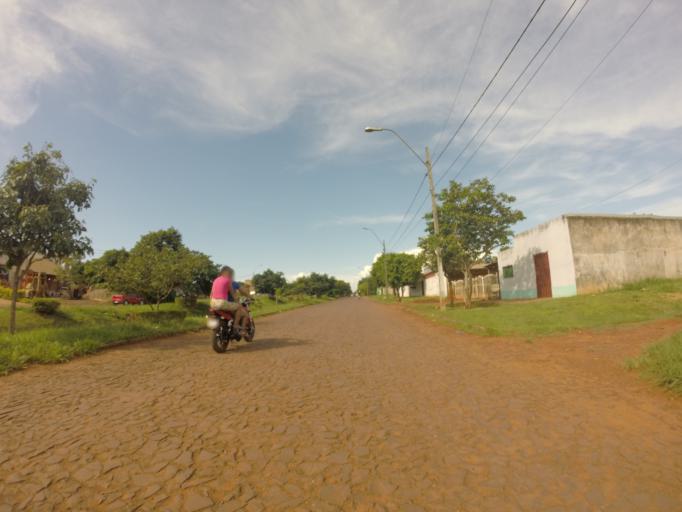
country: PY
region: Alto Parana
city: Ciudad del Este
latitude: -25.3924
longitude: -54.6454
